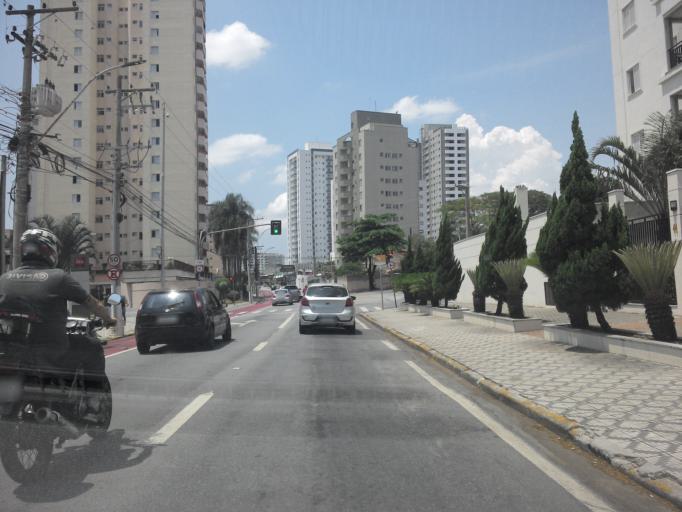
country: BR
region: Sao Paulo
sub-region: Taubate
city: Taubate
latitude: -23.0359
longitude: -45.5720
